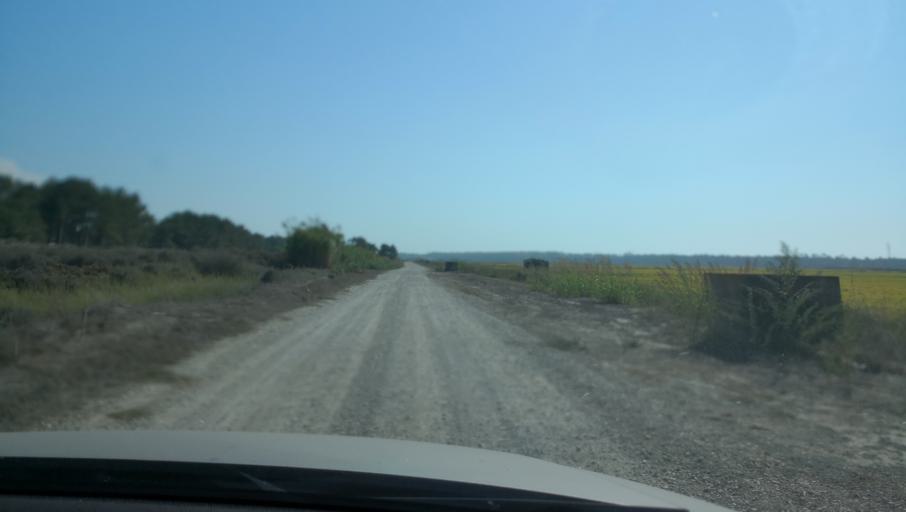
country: PT
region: Setubal
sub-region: Setubal
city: Setubal
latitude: 38.3968
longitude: -8.7880
